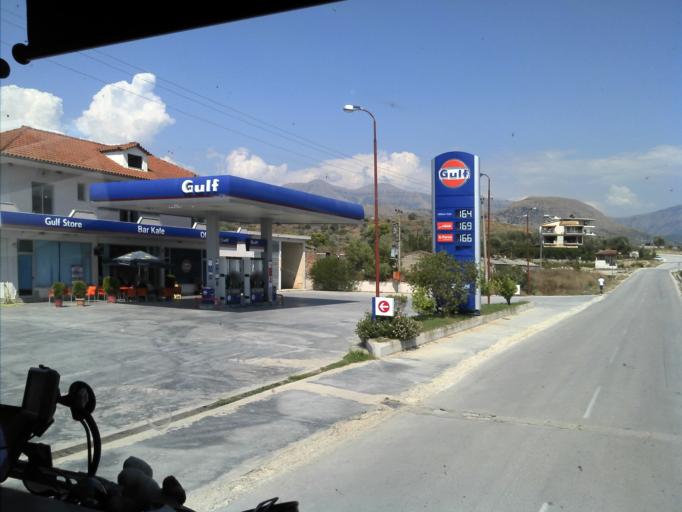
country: AL
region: Vlore
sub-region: Rrethi i Delvines
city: Finiq
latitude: 39.8976
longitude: 20.0744
